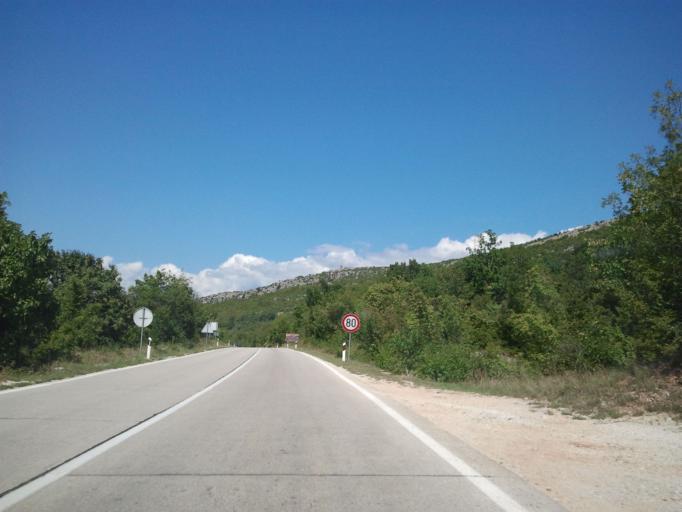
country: HR
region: Zadarska
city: Krusevo
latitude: 44.1651
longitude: 15.6264
